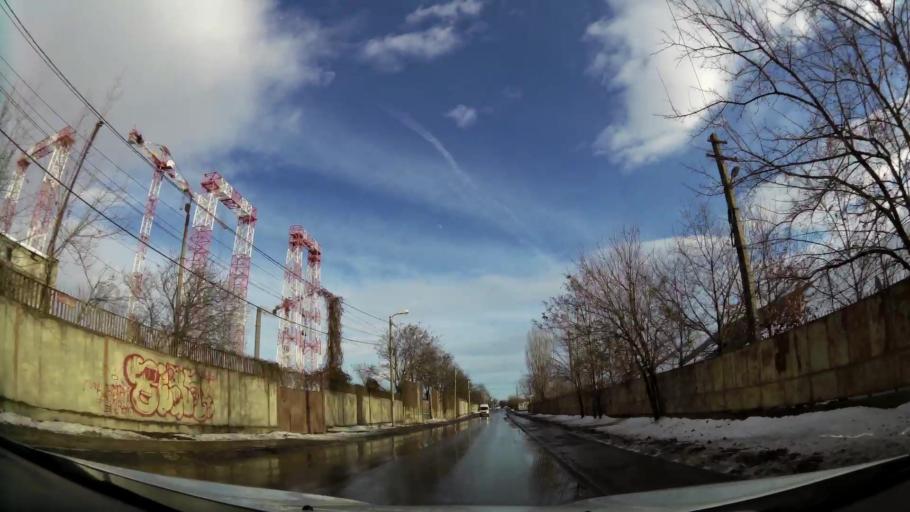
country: RO
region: Ilfov
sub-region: Comuna Jilava
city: Jilava
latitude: 44.3682
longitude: 26.0949
